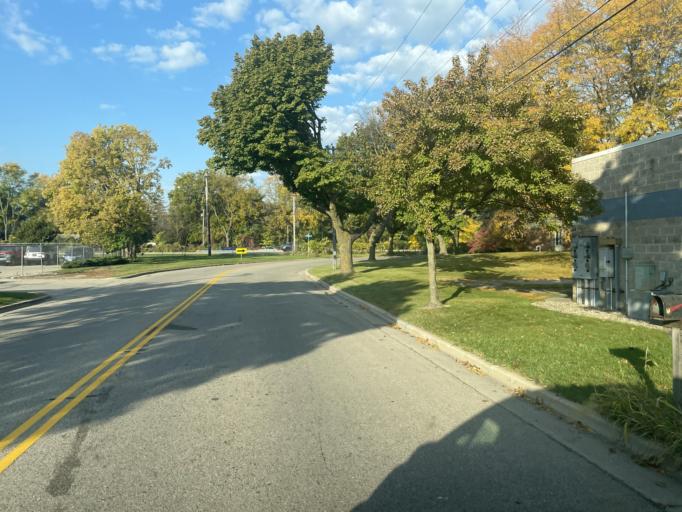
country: US
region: Wisconsin
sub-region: Dane County
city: Monona
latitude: 43.0932
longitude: -89.3133
